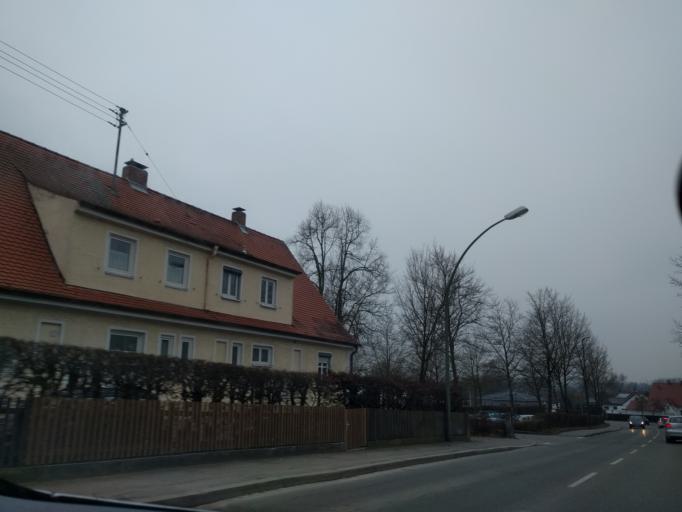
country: DE
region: Bavaria
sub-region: Swabia
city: Donauwoerth
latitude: 48.7244
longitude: 10.7757
